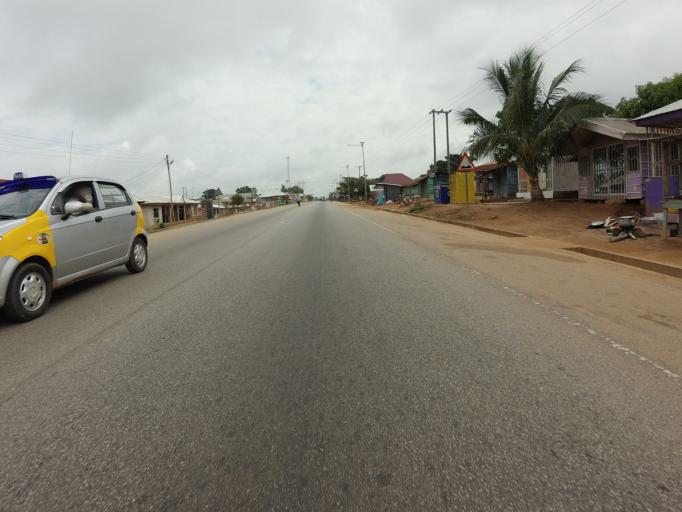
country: GH
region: Ashanti
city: Tafo
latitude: 6.9672
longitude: -1.6812
